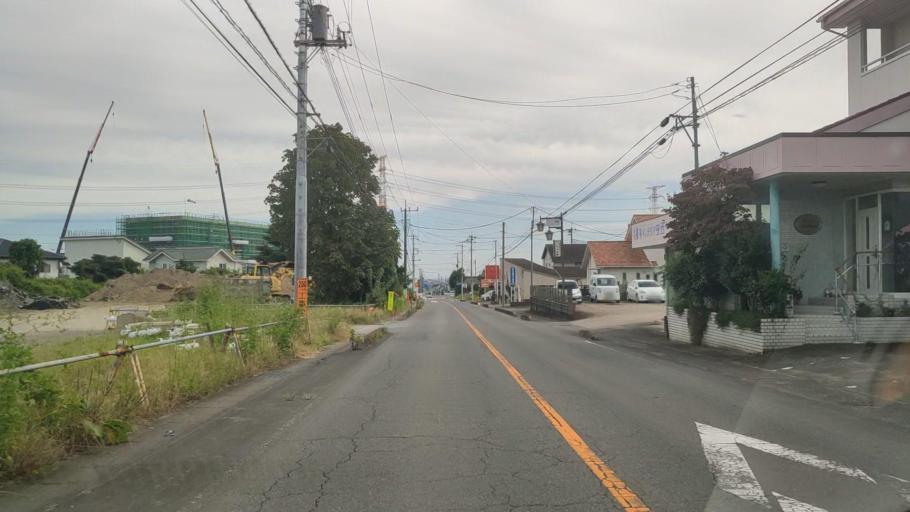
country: JP
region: Gunma
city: Kanekomachi
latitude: 36.3821
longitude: 138.9641
